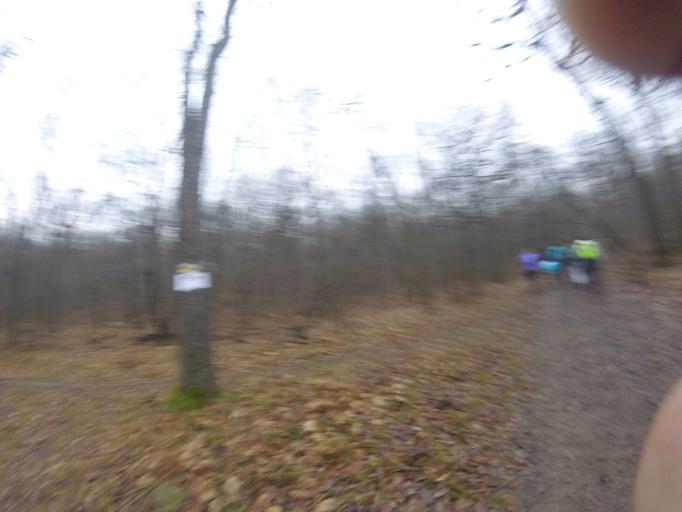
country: HU
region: Pest
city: Budakeszi
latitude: 47.5448
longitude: 18.9766
